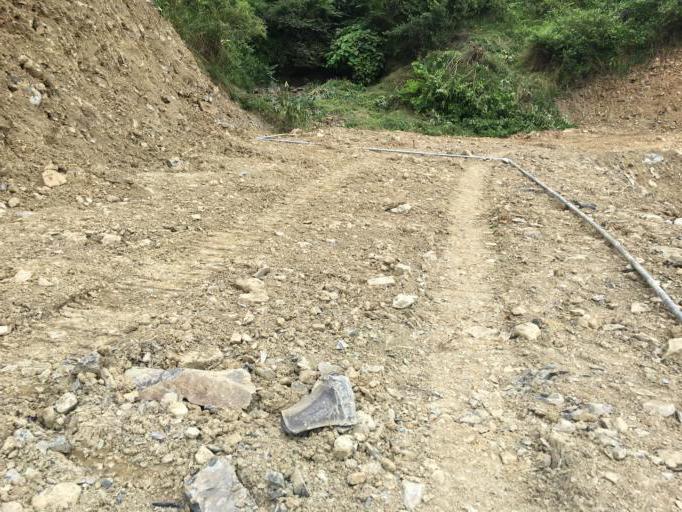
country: CN
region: Guangxi Zhuangzu Zizhiqu
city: Tongle
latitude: 25.1233
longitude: 106.4224
